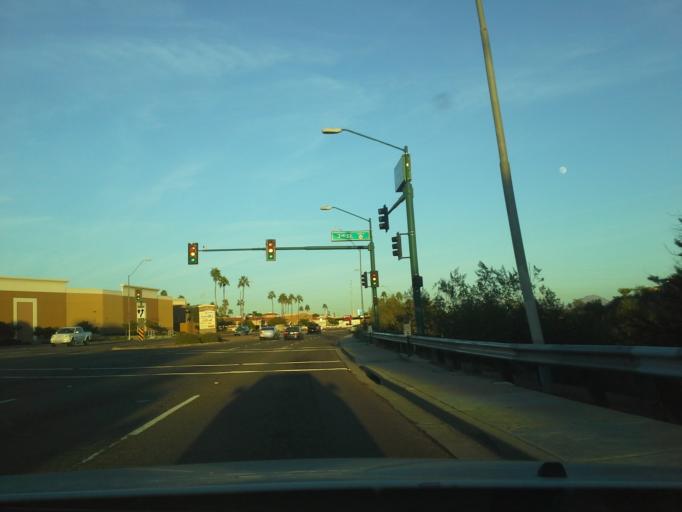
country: US
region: Arizona
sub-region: Maricopa County
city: Glendale
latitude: 33.6364
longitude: -112.0697
